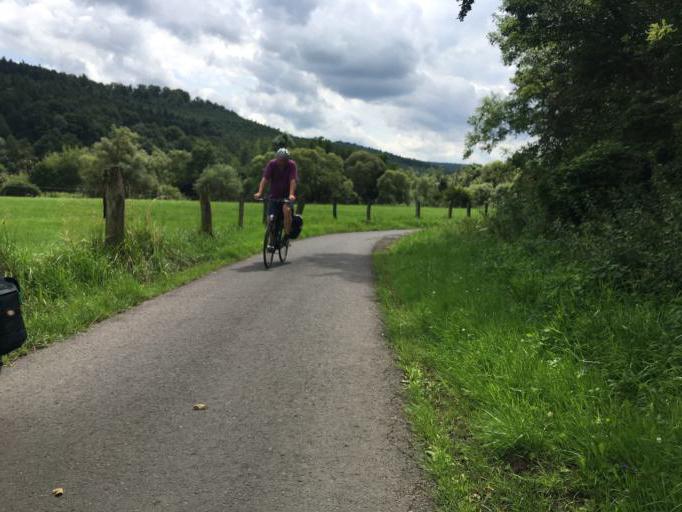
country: DE
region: Hesse
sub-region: Regierungsbezirk Darmstadt
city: Gelnhausen
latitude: 50.2207
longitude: 9.2405
